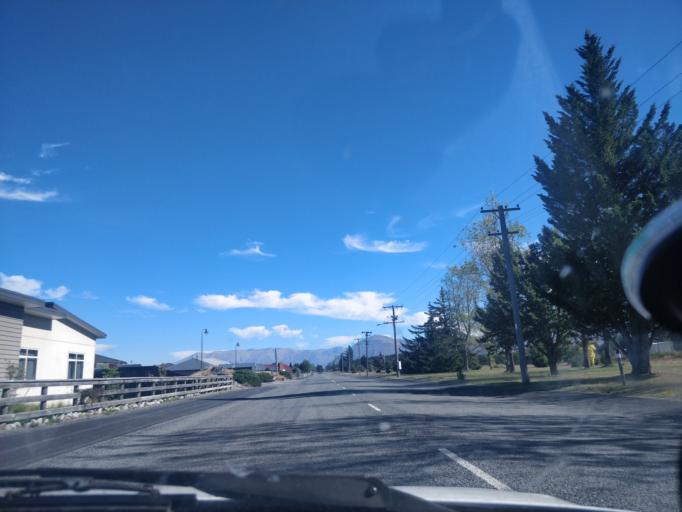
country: NZ
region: Canterbury
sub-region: Timaru District
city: Pleasant Point
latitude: -44.2642
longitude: 170.0968
